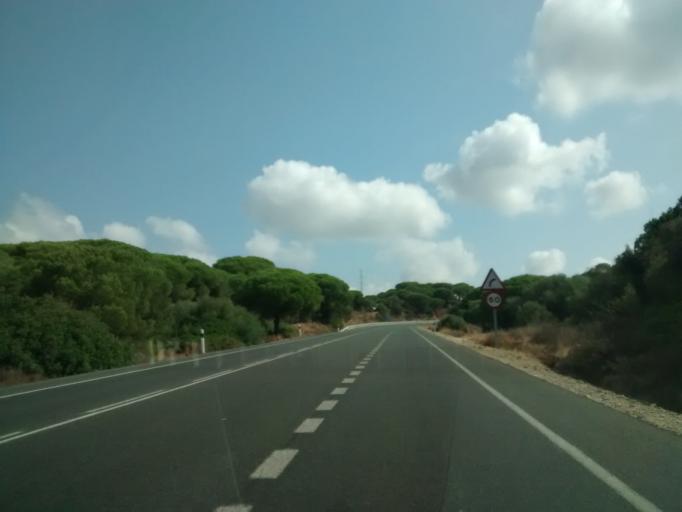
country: ES
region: Andalusia
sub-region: Provincia de Cadiz
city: Vejer de la Frontera
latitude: 36.2542
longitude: -5.9491
